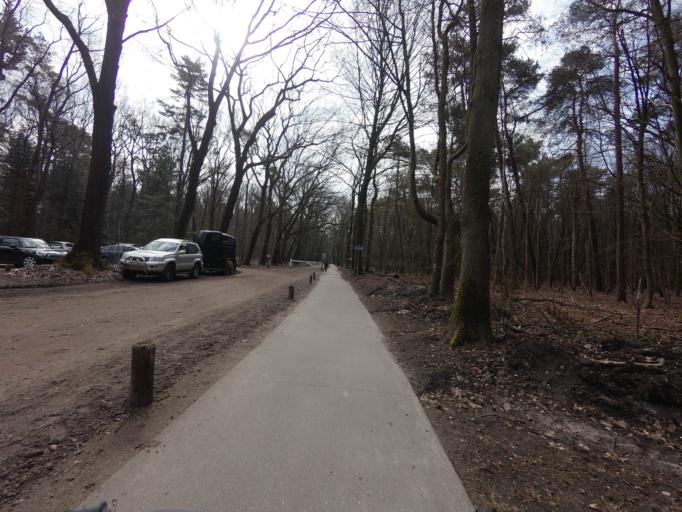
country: NL
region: Gelderland
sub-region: Gemeente Harderwijk
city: Harderwijk
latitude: 52.3426
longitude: 5.7074
